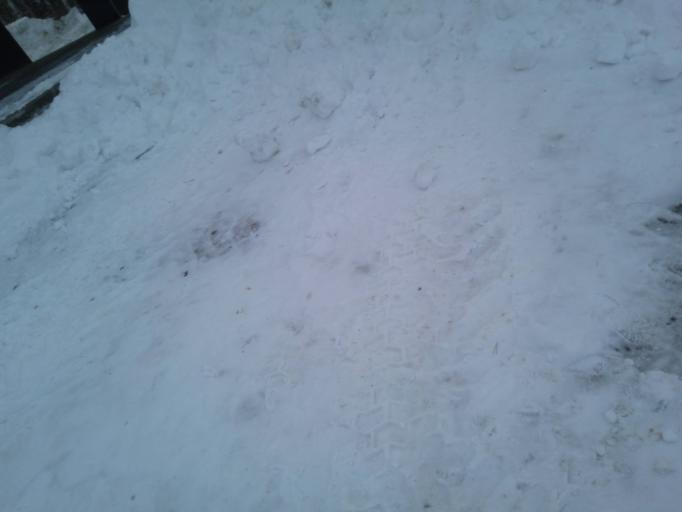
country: RU
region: Novosibirsk
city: Akademgorodok
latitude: 54.8360
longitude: 83.1007
